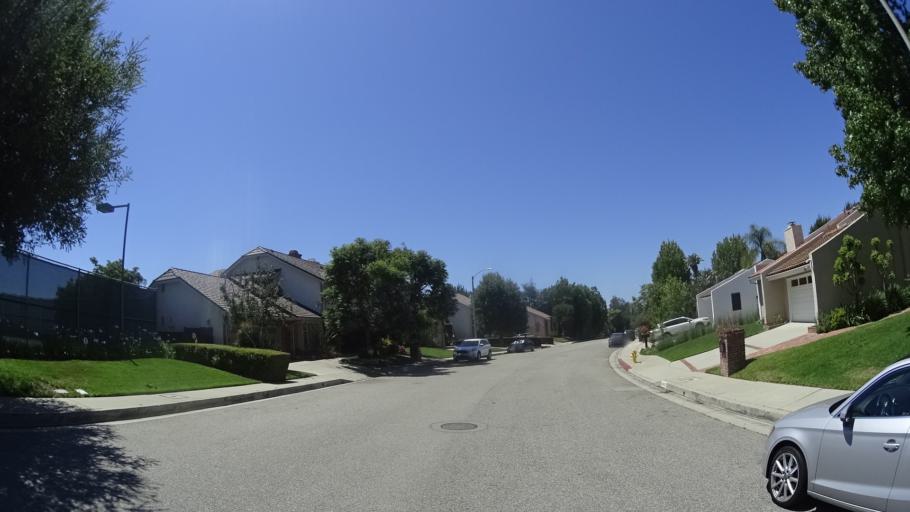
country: US
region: California
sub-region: Los Angeles County
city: Sherman Oaks
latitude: 34.1192
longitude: -118.4425
